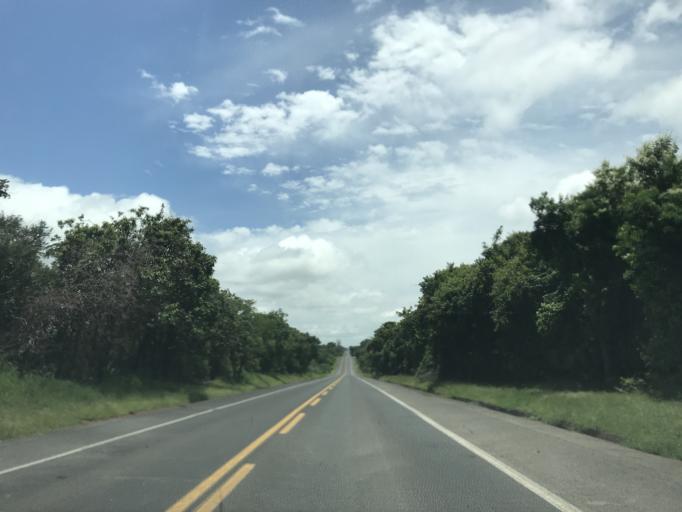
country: BR
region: Minas Gerais
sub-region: Prata
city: Prata
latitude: -19.6279
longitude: -48.9494
